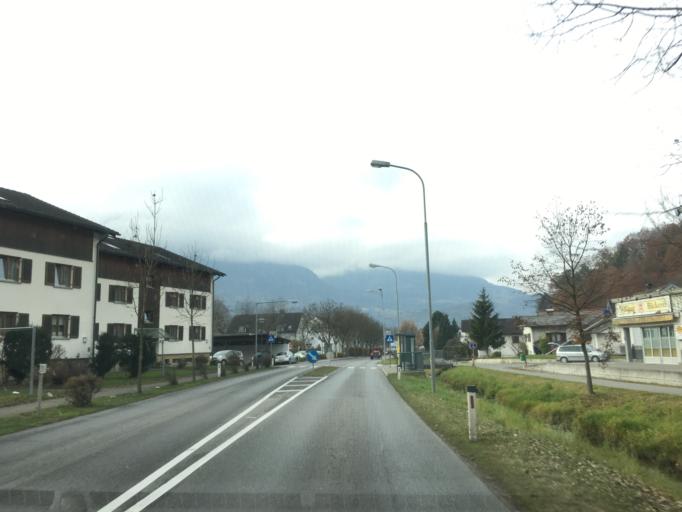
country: AT
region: Vorarlberg
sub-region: Politischer Bezirk Bludenz
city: Bludesch
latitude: 47.1969
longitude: 9.7224
